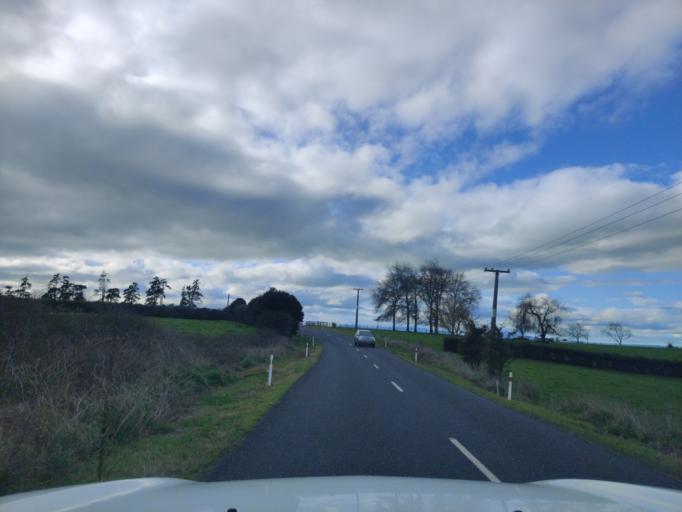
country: NZ
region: Waikato
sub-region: Hauraki District
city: Paeroa
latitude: -37.5895
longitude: 175.5073
